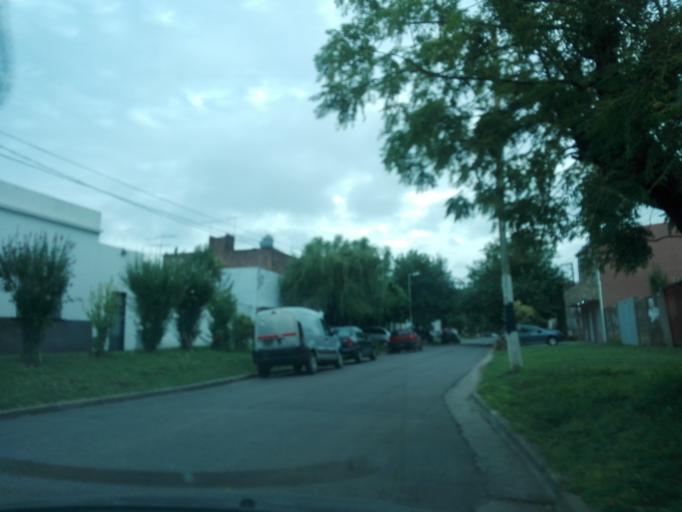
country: AR
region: Buenos Aires
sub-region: Partido de La Plata
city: La Plata
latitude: -34.9380
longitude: -57.9789
